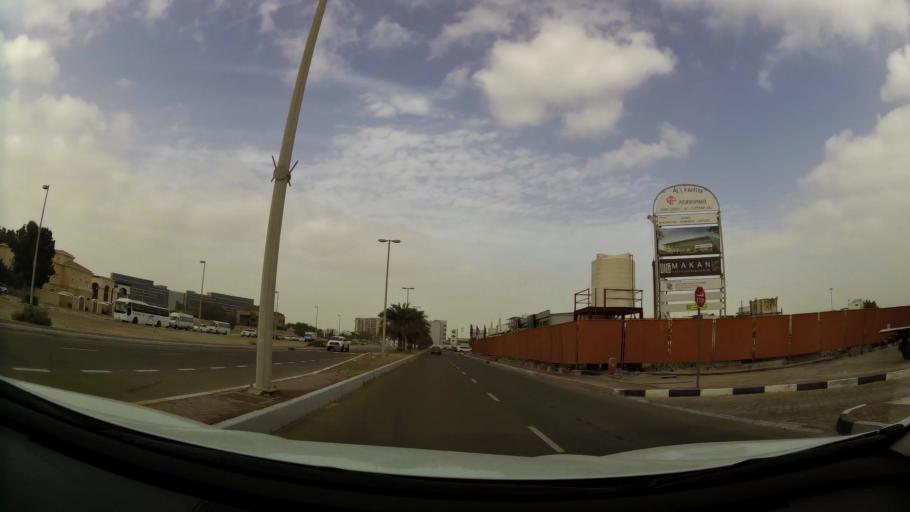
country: AE
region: Abu Dhabi
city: Abu Dhabi
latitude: 24.4155
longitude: 54.4961
